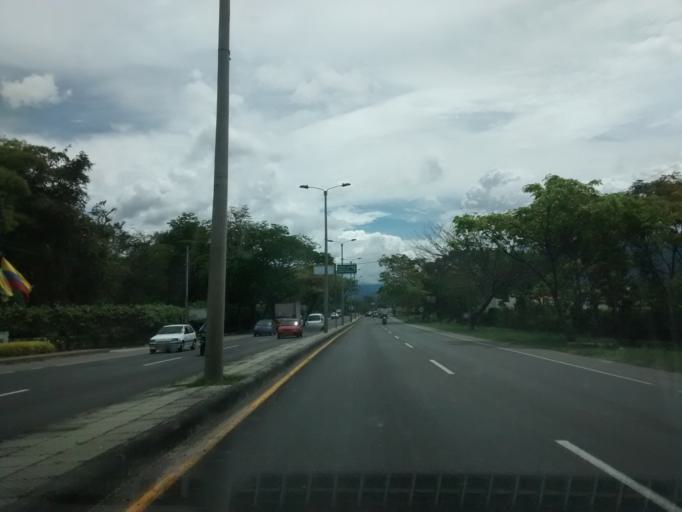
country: CO
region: Tolima
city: Ibague
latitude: 4.4047
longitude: -75.1623
